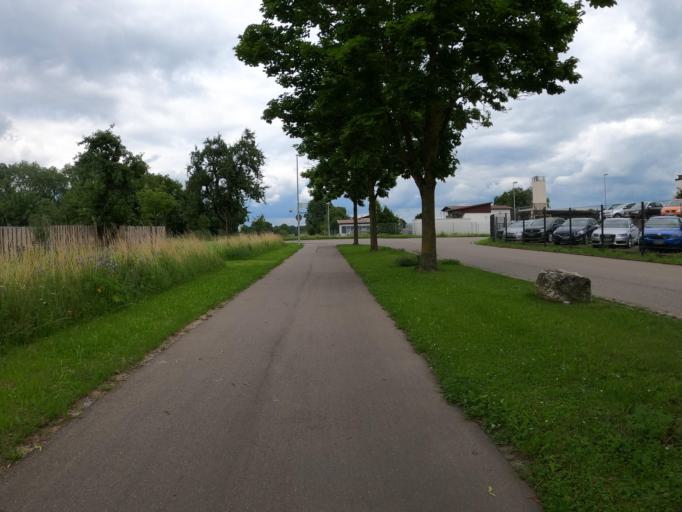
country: DE
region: Baden-Wuerttemberg
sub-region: Tuebingen Region
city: Langenau
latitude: 48.5004
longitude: 10.1380
